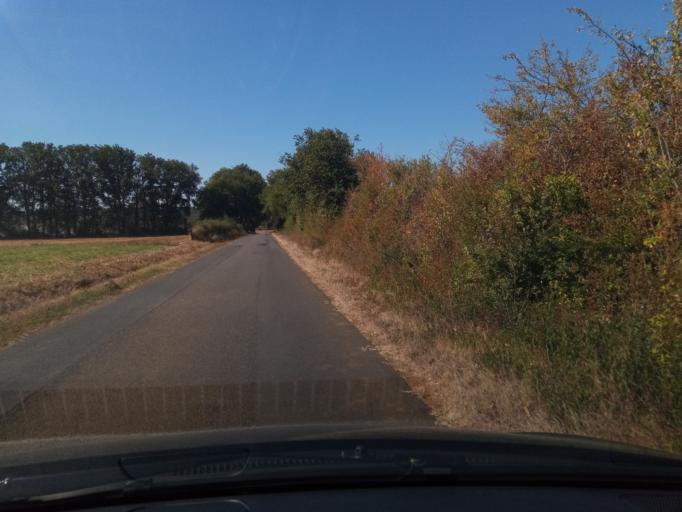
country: FR
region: Poitou-Charentes
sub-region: Departement de la Vienne
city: Montmorillon
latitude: 46.4814
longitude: 0.8547
